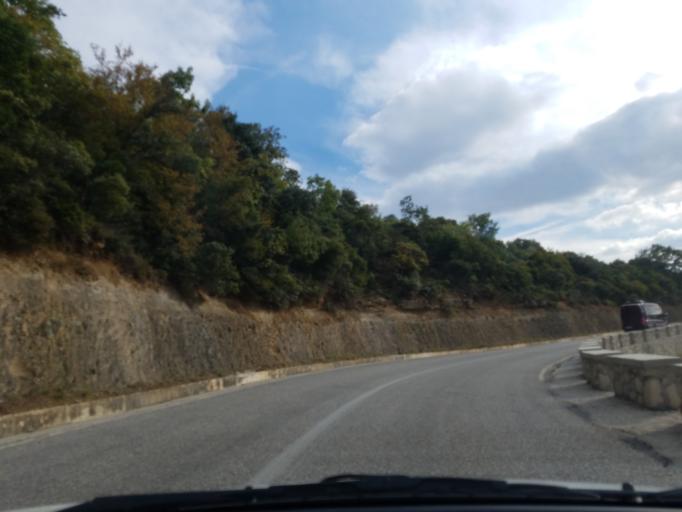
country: GR
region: Thessaly
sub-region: Trikala
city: Kalampaka
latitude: 39.7123
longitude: 21.6383
